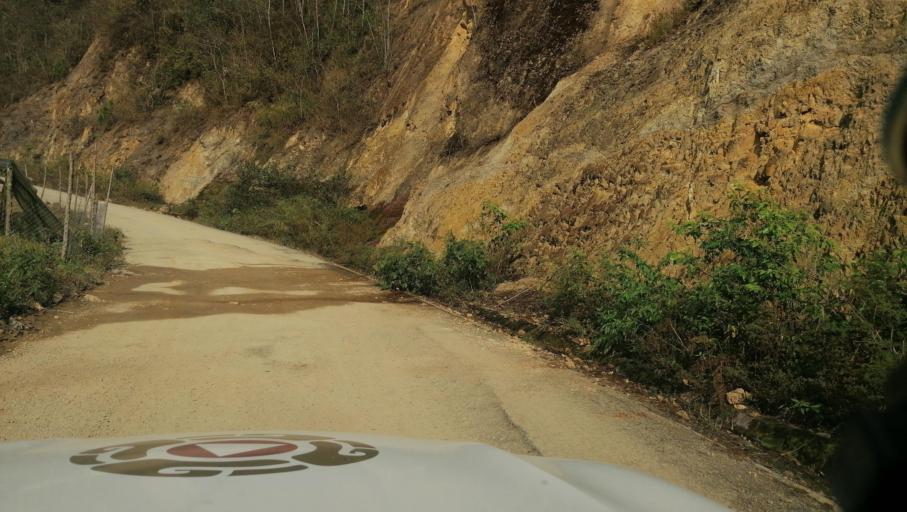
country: GT
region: San Marcos
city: Tacana
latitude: 15.2240
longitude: -92.1931
